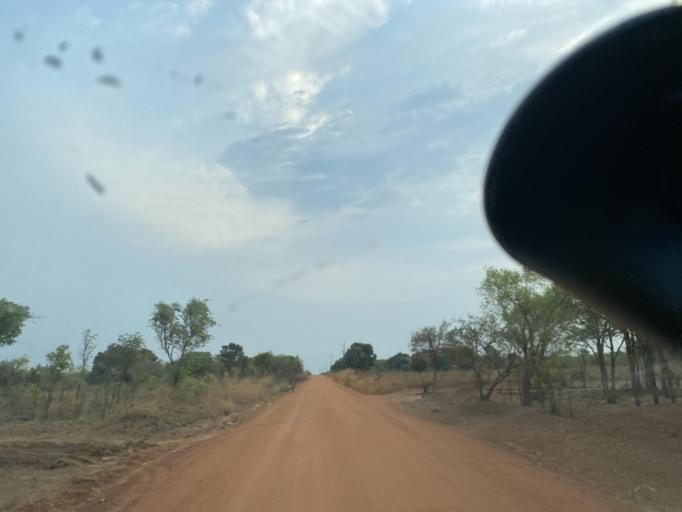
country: ZM
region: Lusaka
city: Chongwe
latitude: -15.2261
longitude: 28.5903
